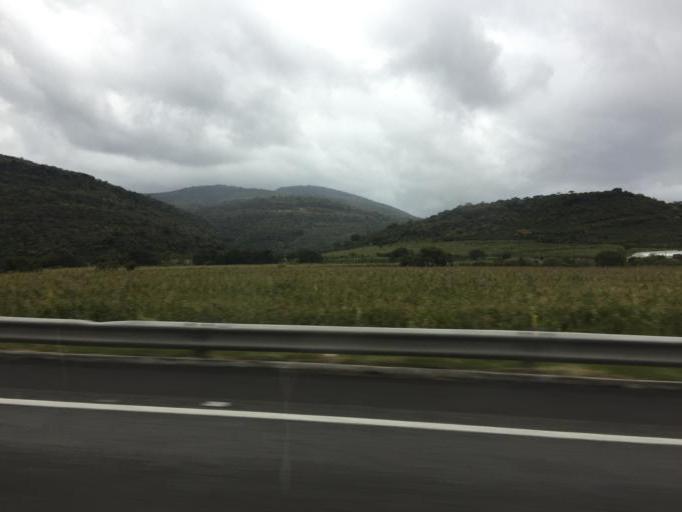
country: MX
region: Jalisco
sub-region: Zapotlanejo
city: La Mezquitera
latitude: 20.5381
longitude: -103.0202
